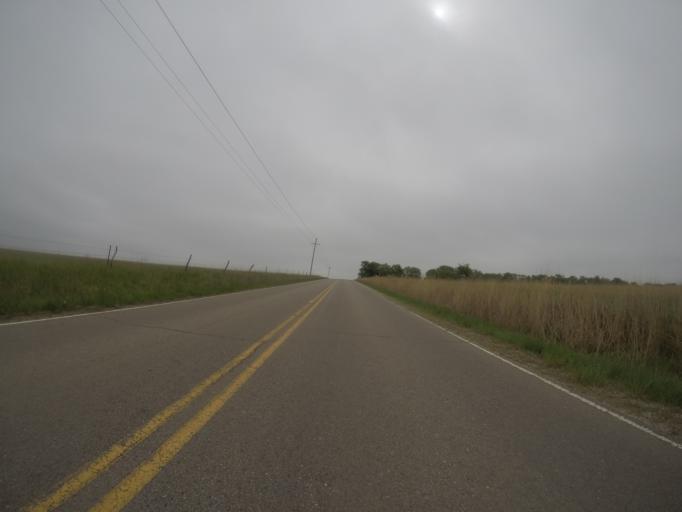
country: US
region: Kansas
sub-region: Pottawatomie County
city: Westmoreland
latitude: 39.5222
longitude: -96.2925
